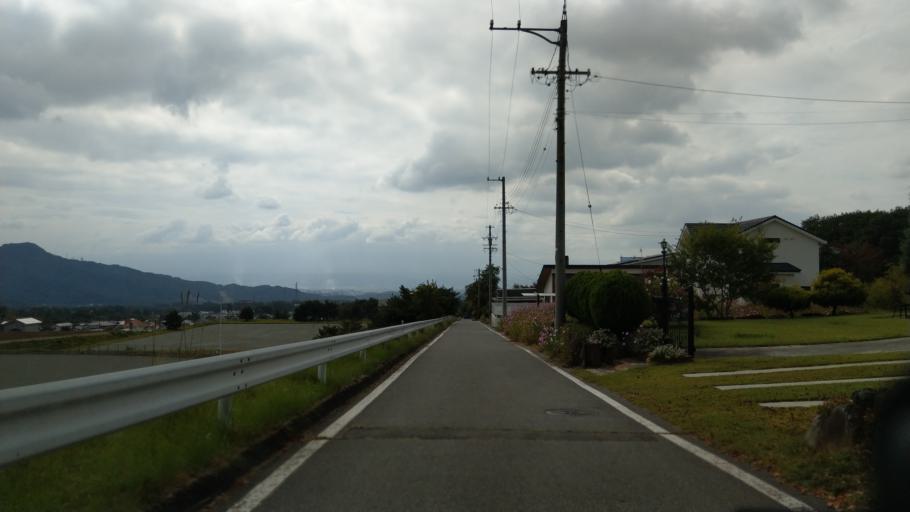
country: JP
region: Nagano
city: Komoro
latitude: 36.3244
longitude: 138.5280
